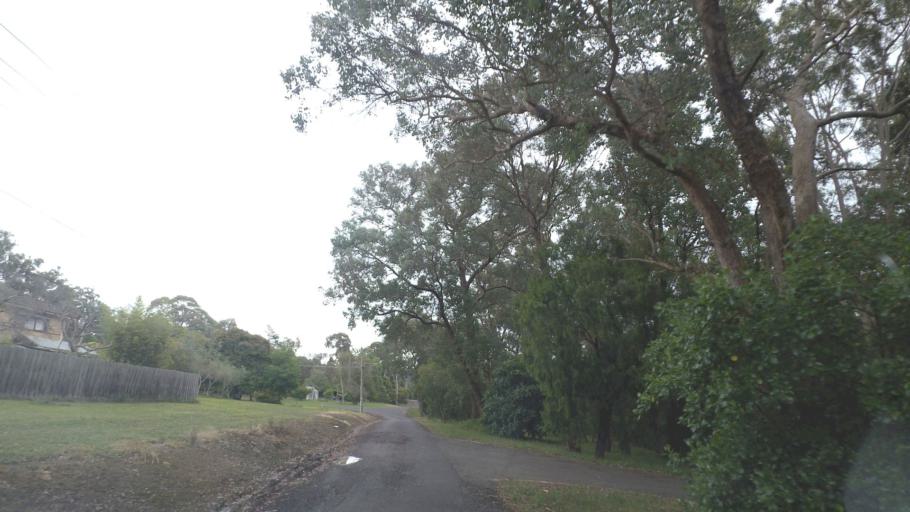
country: AU
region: Victoria
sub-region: Manningham
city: Park Orchards
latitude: -37.7765
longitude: 145.2149
